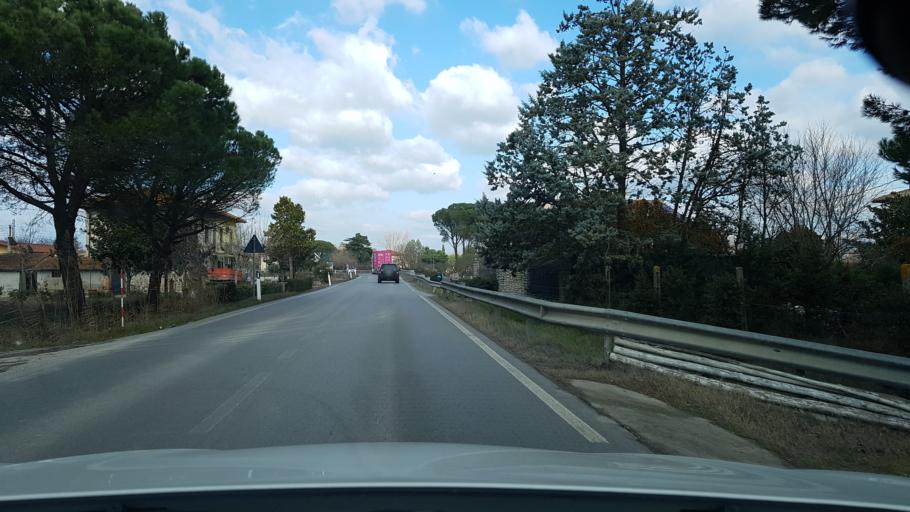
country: IT
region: Umbria
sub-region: Provincia di Perugia
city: Castiglione del Lago
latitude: 43.1517
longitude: 12.0206
